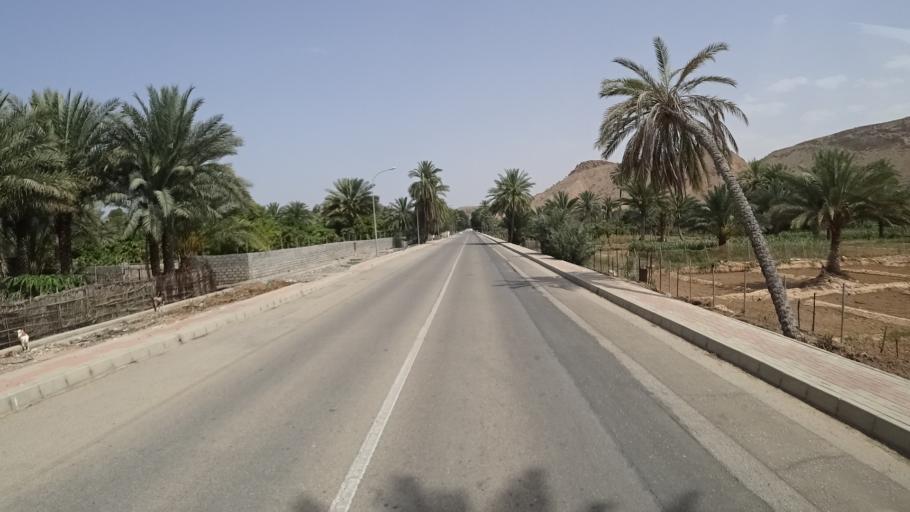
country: OM
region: Muhafazat Masqat
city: Muscat
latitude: 23.1711
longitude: 58.9157
